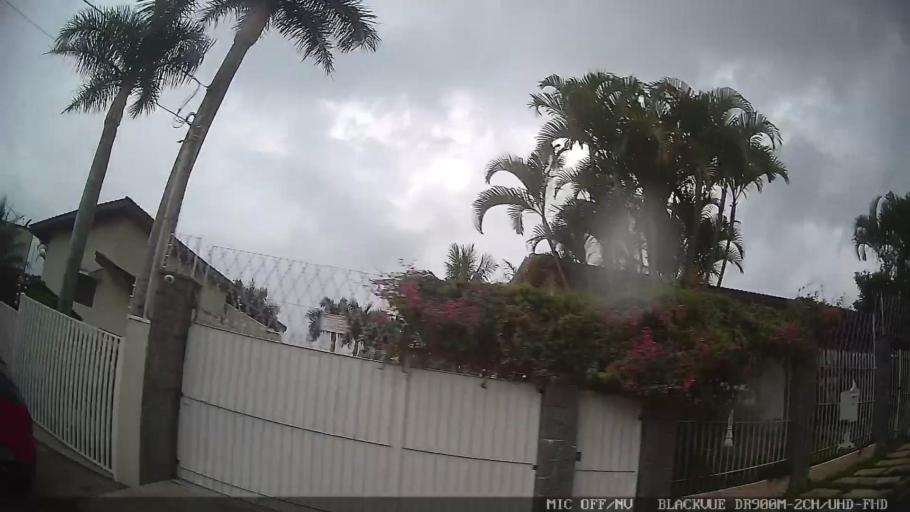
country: BR
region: Sao Paulo
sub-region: Mogi das Cruzes
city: Mogi das Cruzes
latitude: -23.5259
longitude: -46.1808
